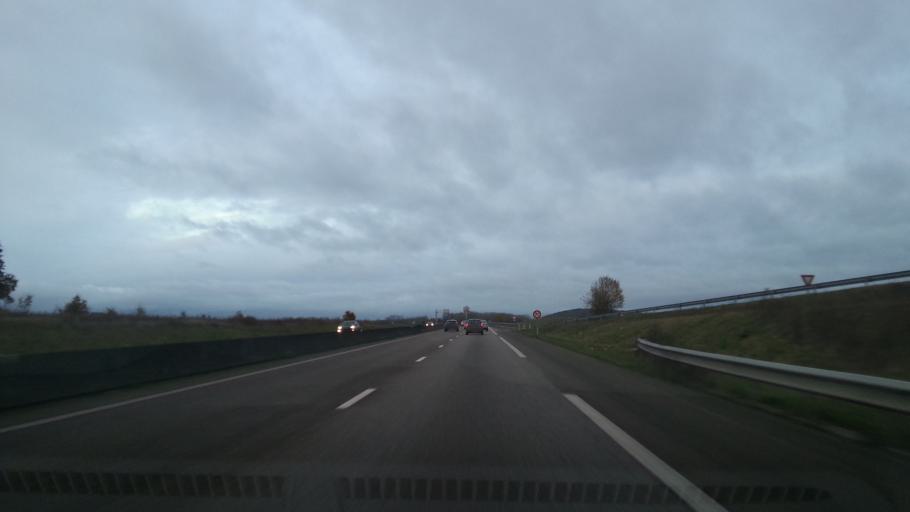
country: FR
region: Picardie
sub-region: Departement de l'Oise
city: Bailleul-sur-Therain
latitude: 49.4129
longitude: 2.2165
